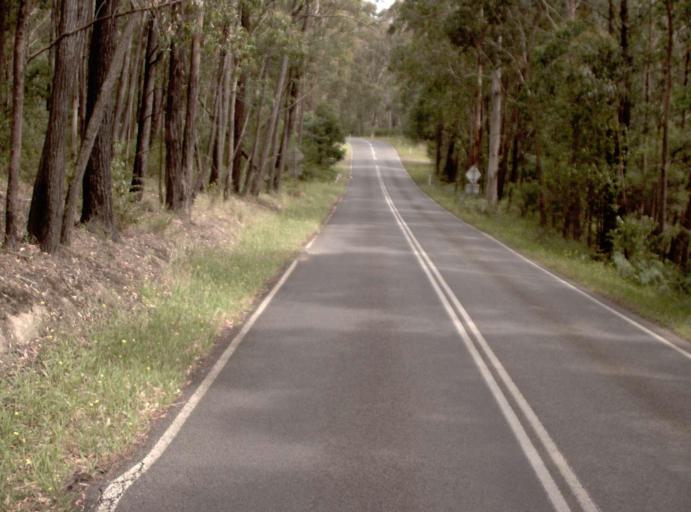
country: AU
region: Victoria
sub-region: Latrobe
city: Traralgon
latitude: -38.0463
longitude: 146.4247
